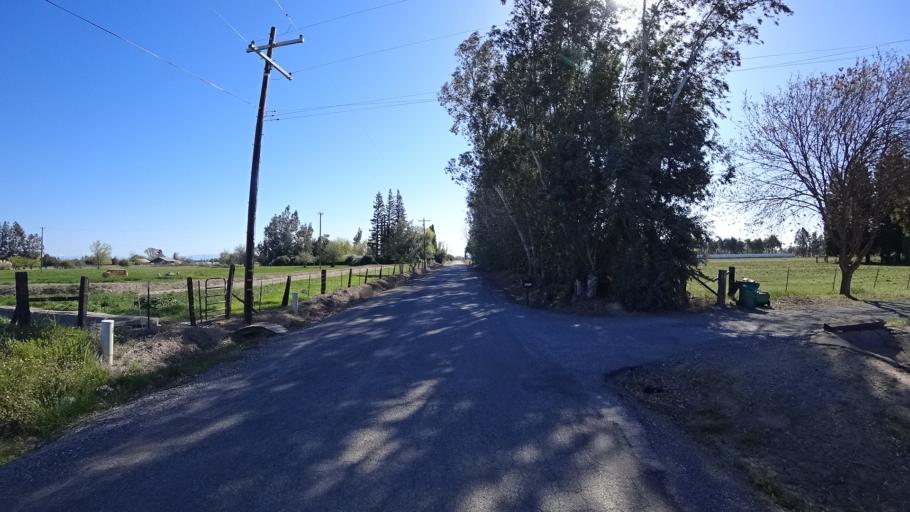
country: US
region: California
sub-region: Glenn County
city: Orland
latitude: 39.7368
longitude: -122.2205
